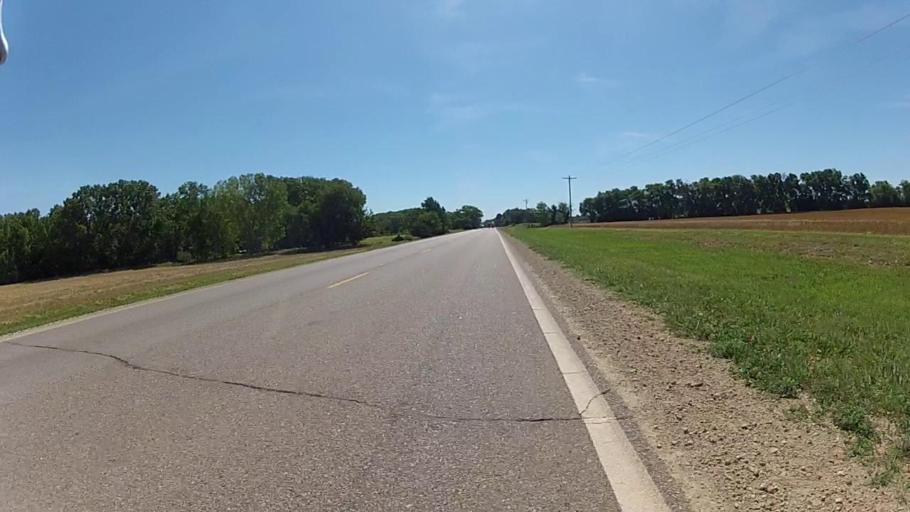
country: US
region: Kansas
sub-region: Barber County
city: Medicine Lodge
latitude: 37.2753
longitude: -98.6097
